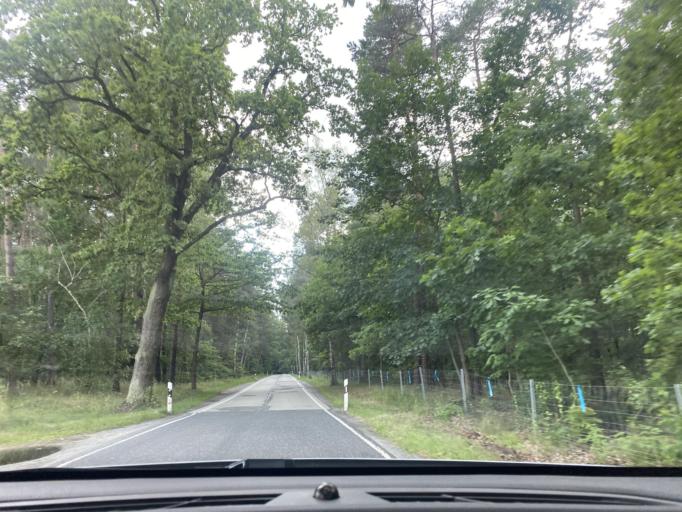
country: DE
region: Saxony
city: Klitten
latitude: 51.3687
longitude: 14.6087
